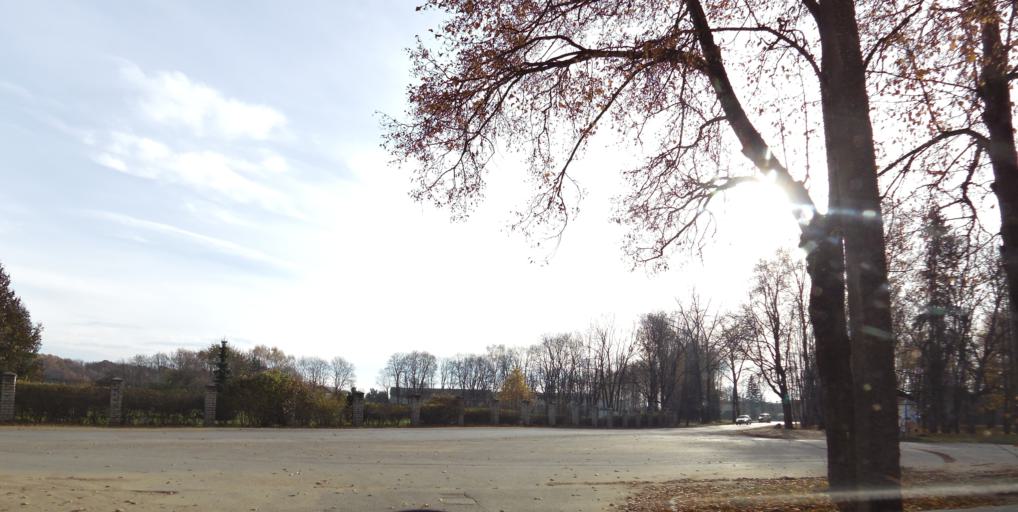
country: LT
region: Vilnius County
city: Justiniskes
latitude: 54.7173
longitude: 25.1965
